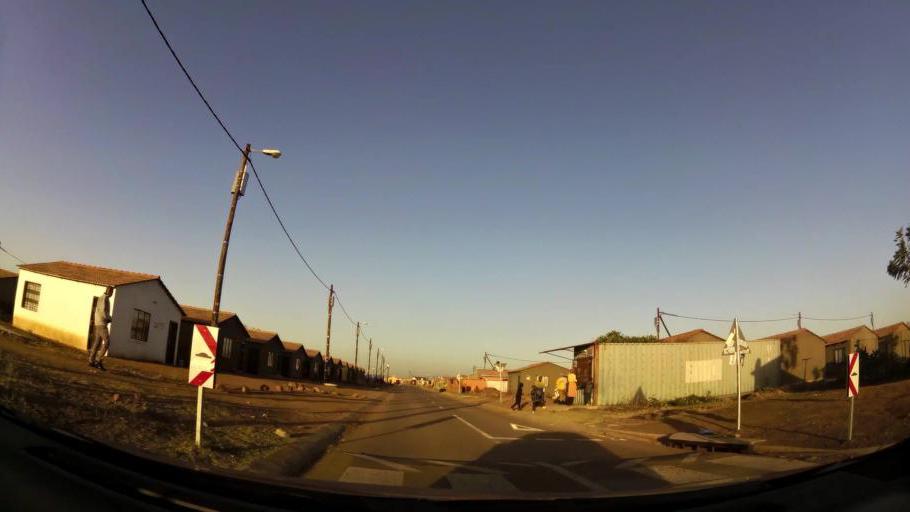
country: ZA
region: North-West
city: Ga-Rankuwa
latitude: -25.6040
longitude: 28.0974
